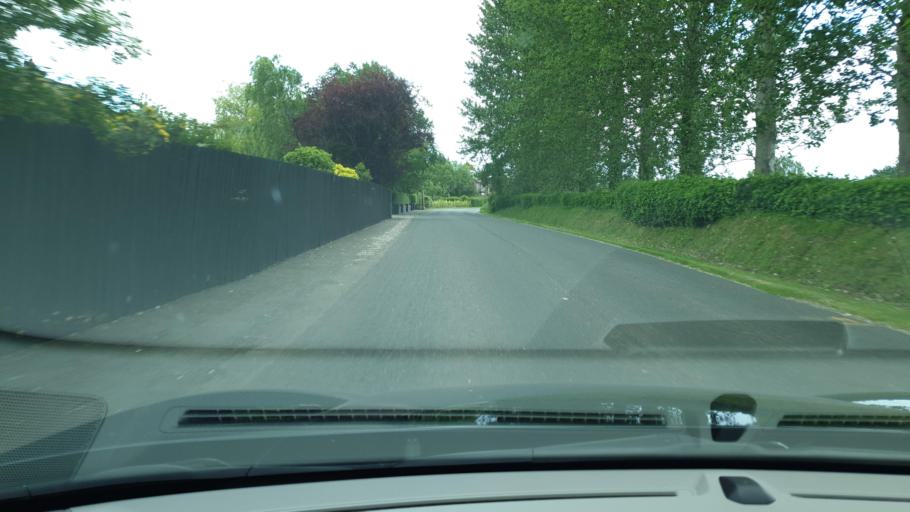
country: IE
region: Leinster
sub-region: An Mhi
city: Dunboyne
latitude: 53.4023
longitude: -6.4698
